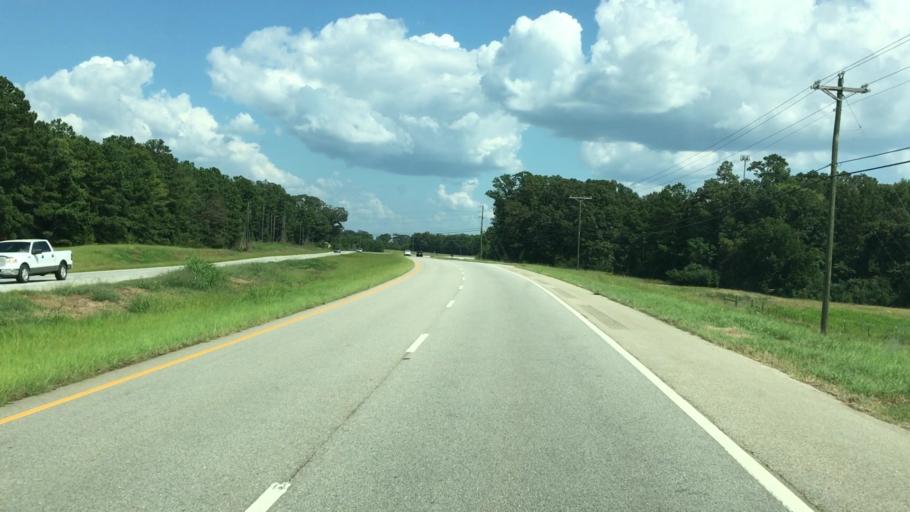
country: US
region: Georgia
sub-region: Putnam County
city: Eatonton
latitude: 33.2701
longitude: -83.3429
